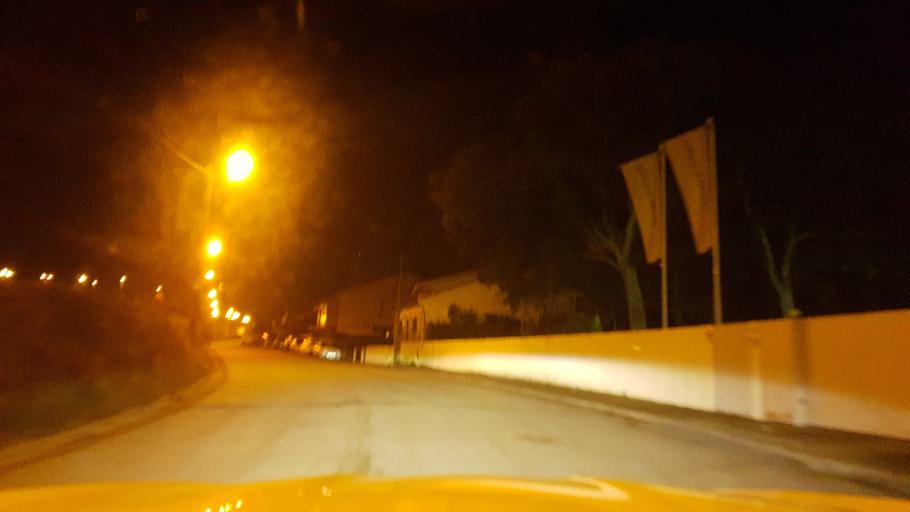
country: PT
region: Porto
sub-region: Matosinhos
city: Senhora da Hora
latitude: 41.2087
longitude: -8.6431
